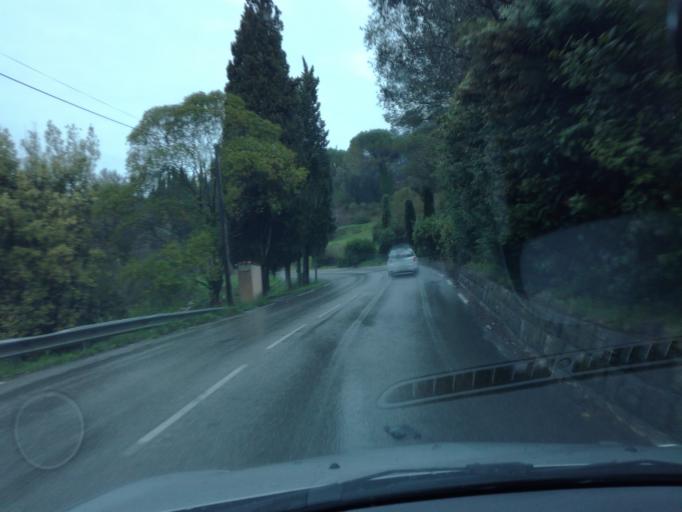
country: FR
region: Provence-Alpes-Cote d'Azur
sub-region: Departement des Alpes-Maritimes
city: Mouans-Sartoux
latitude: 43.6329
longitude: 6.9750
